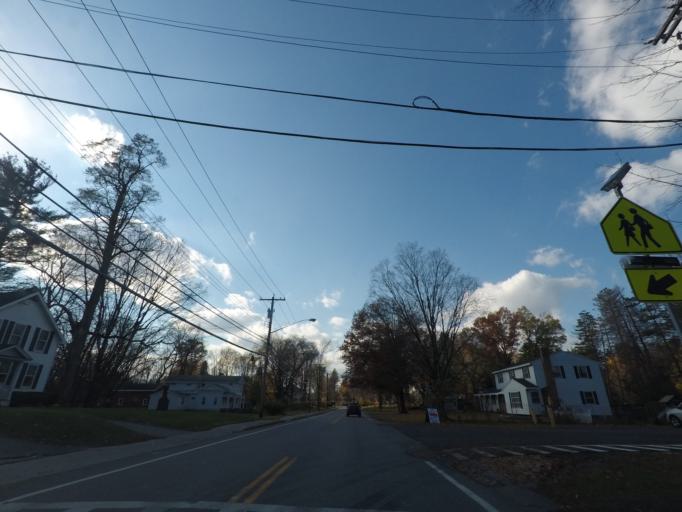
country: US
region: New York
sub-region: Schenectady County
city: East Glenville
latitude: 42.9101
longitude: -73.8918
